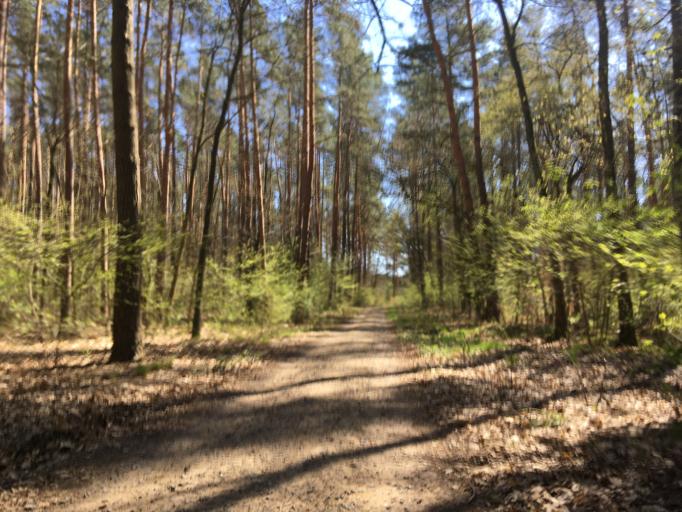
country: DE
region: Brandenburg
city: Bernau bei Berlin
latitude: 52.6996
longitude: 13.5381
